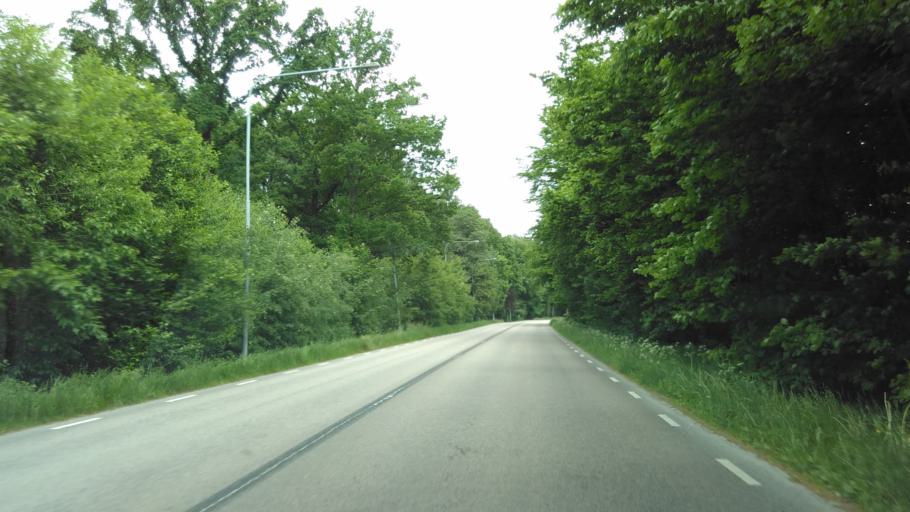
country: SE
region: Vaestra Goetaland
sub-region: Lidkopings Kommun
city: Lidkoping
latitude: 58.4849
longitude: 13.1379
